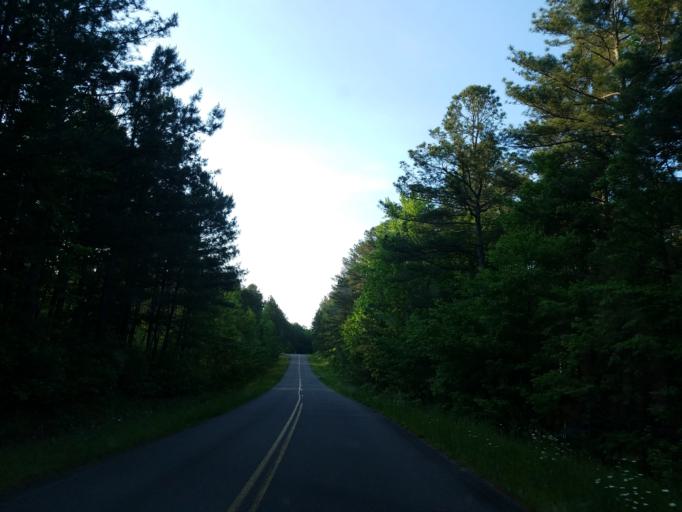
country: US
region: Georgia
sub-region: Gordon County
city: Calhoun
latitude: 34.6251
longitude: -85.0796
